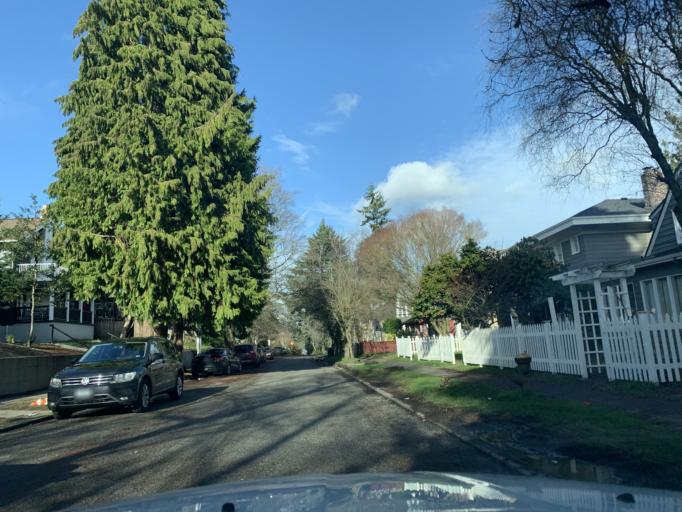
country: US
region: Washington
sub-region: King County
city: Seattle
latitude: 47.6656
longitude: -122.3071
